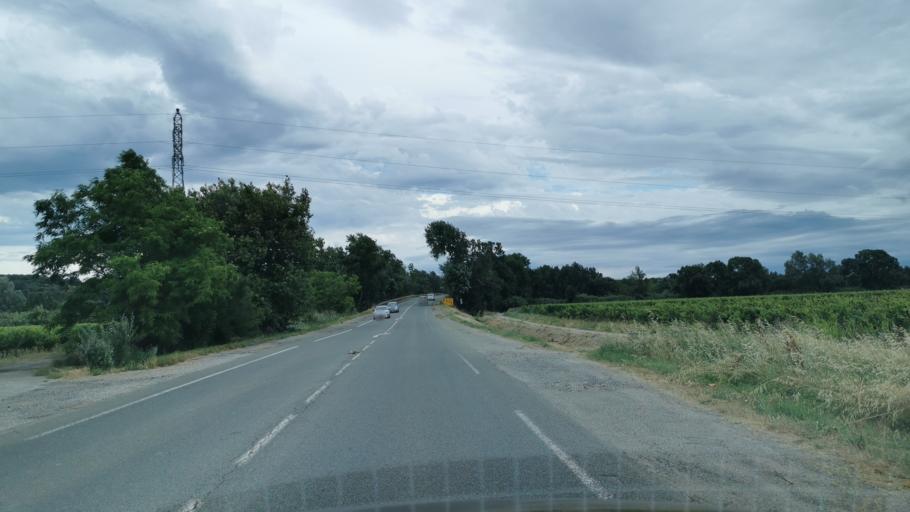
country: FR
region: Languedoc-Roussillon
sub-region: Departement de l'Aude
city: Marcorignan
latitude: 43.2370
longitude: 2.9258
